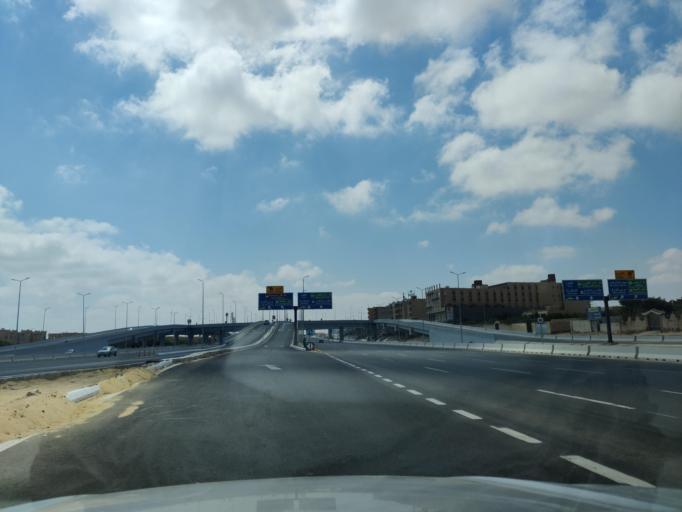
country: EG
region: Muhafazat Matruh
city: Al `Alamayn
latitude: 30.8406
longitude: 28.9505
